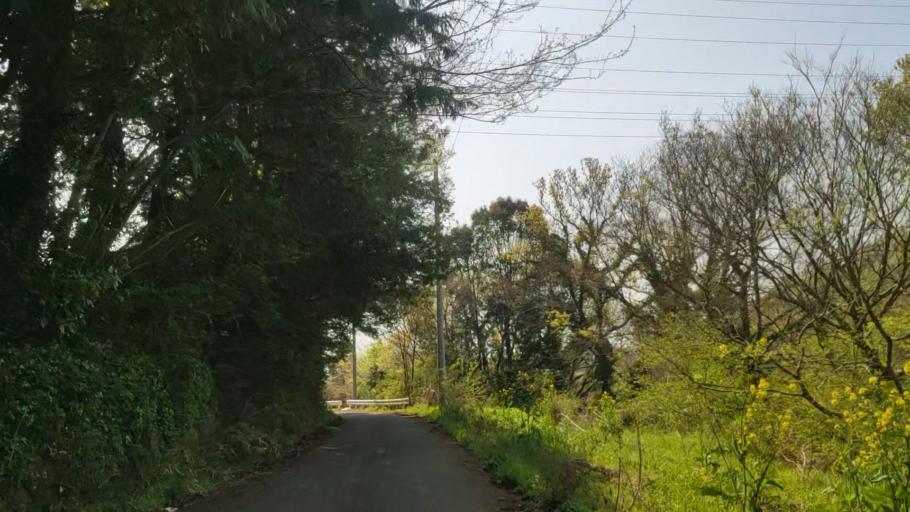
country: JP
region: Kanagawa
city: Ninomiya
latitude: 35.3217
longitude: 139.2720
